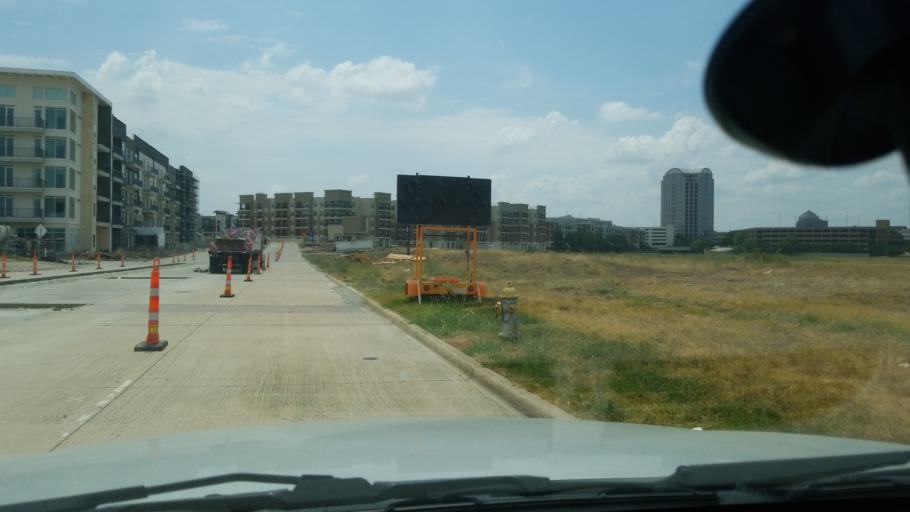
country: US
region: Texas
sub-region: Dallas County
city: Irving
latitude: 32.8753
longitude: -96.9389
